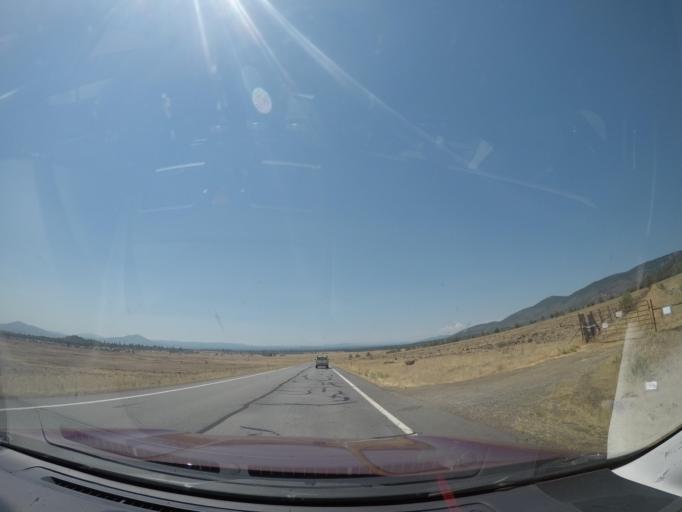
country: US
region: California
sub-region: Shasta County
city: Burney
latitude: 41.0976
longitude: -121.2863
